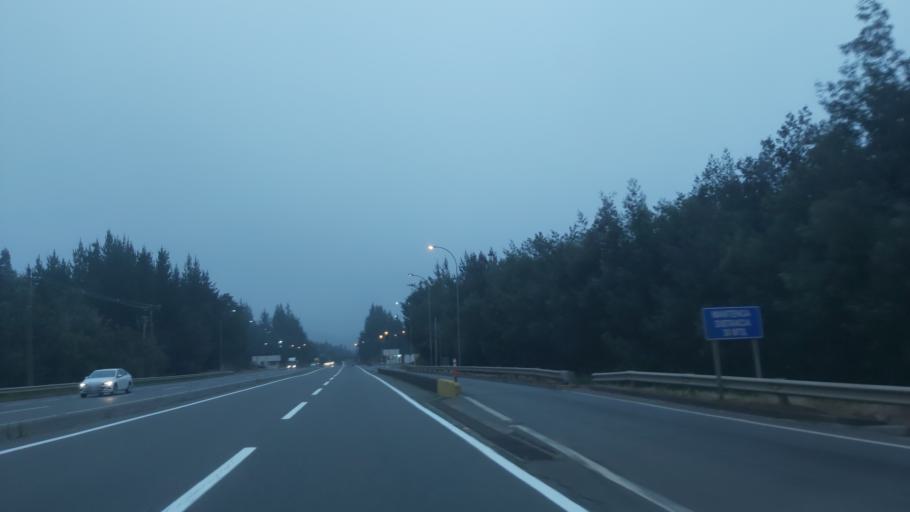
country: CL
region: Biobio
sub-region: Provincia de Concepcion
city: Penco
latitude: -36.7344
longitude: -72.8861
